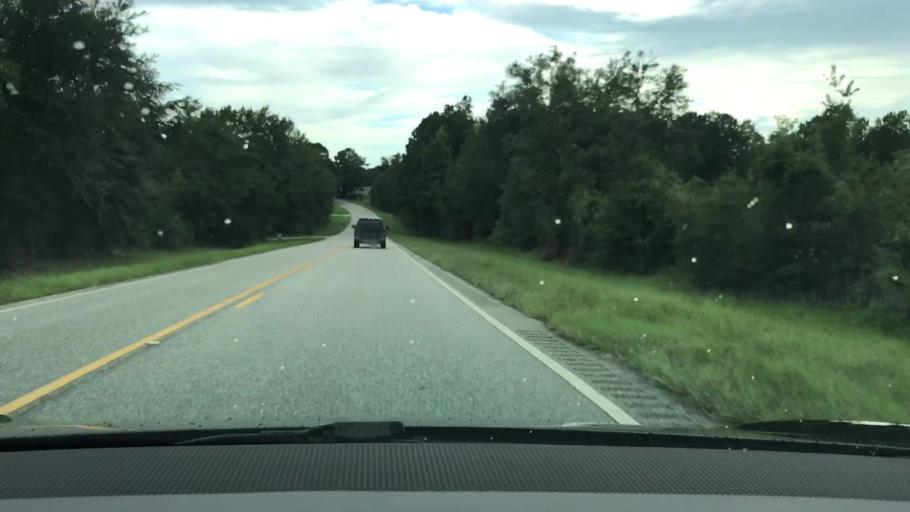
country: US
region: Alabama
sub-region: Geneva County
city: Samson
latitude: 31.0044
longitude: -86.1298
